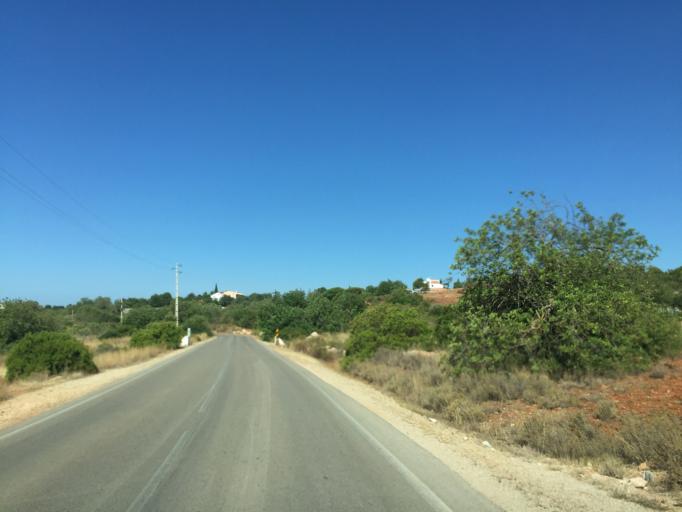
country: PT
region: Faro
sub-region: Loule
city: Vilamoura
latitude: 37.1161
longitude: -8.0775
